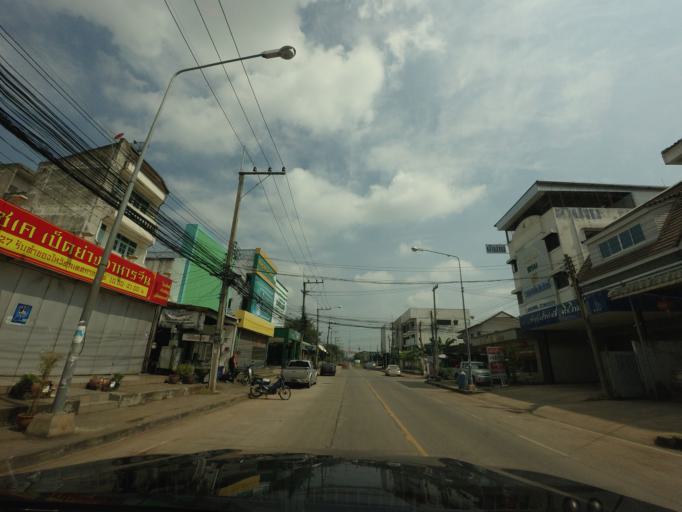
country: TH
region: Khon Kaen
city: Khon Kaen
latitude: 16.4325
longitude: 102.8290
